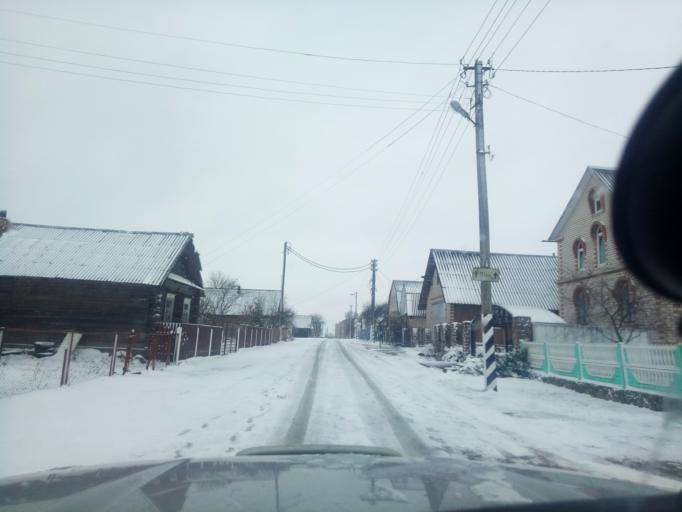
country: BY
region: Minsk
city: Kapyl'
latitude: 53.1537
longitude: 27.0821
